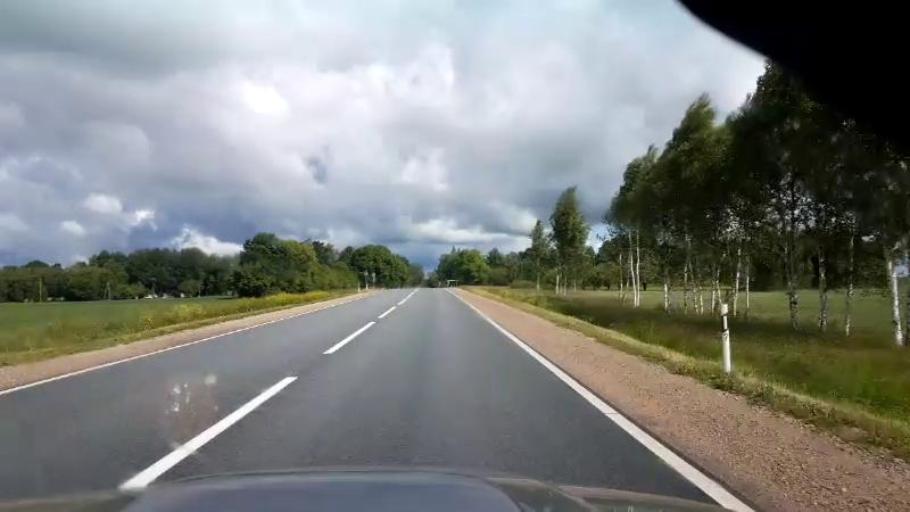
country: LV
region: Lecava
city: Iecava
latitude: 56.5255
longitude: 24.1713
